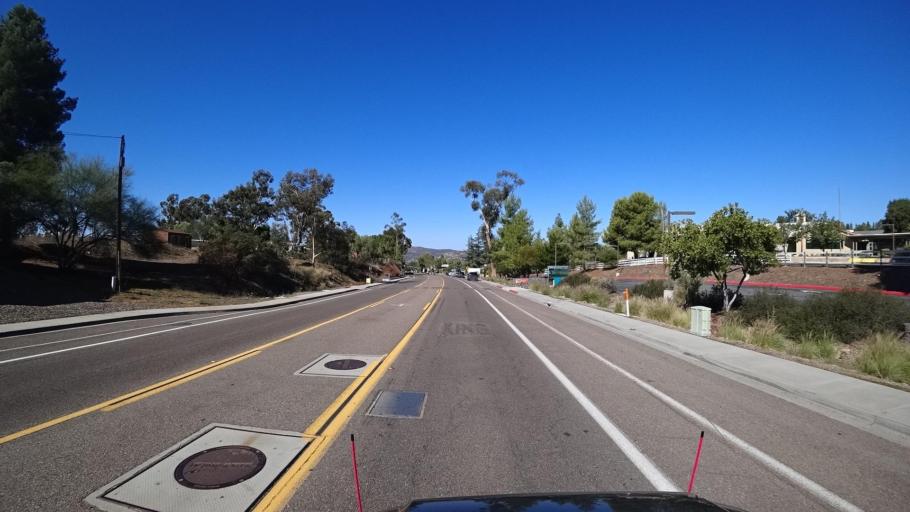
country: US
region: California
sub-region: San Diego County
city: Alpine
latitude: 32.8374
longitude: -116.7737
